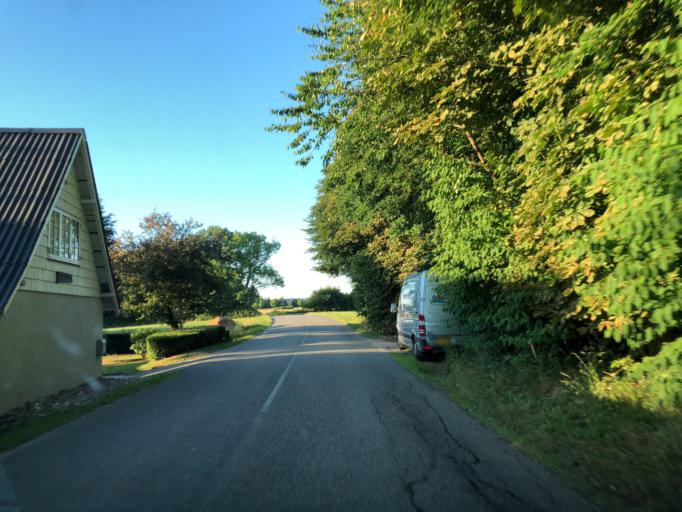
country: DK
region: South Denmark
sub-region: Vejle Kommune
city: Borkop
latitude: 55.6332
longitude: 9.6254
